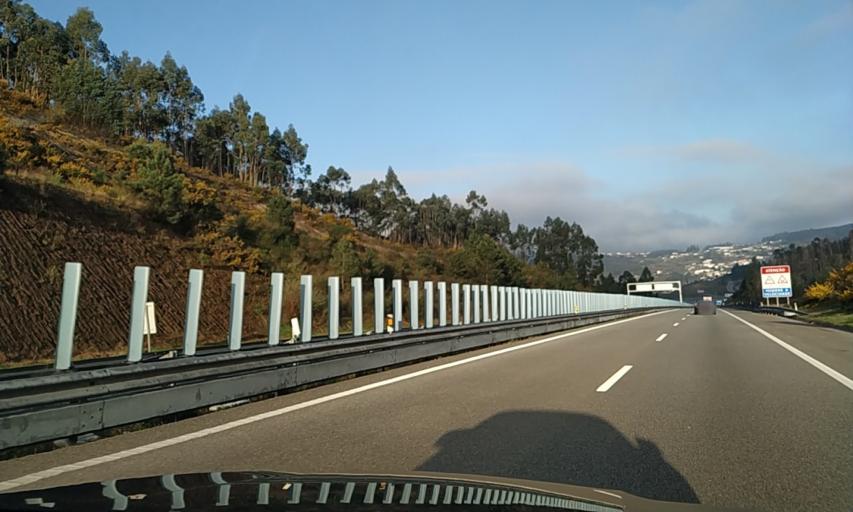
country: PT
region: Porto
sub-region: Lousada
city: Lousada
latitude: 41.2927
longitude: -8.2906
